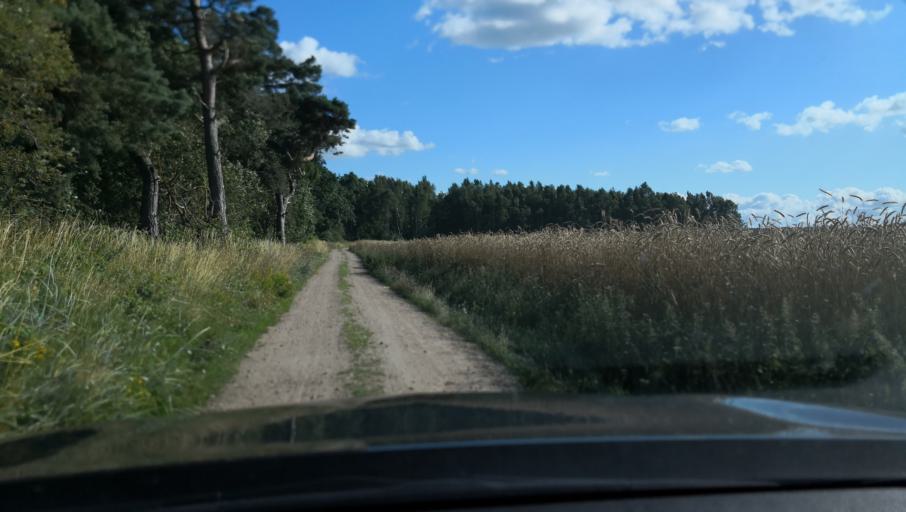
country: SE
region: Skane
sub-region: Kristianstads Kommun
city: Degeberga
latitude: 55.8007
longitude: 14.1956
